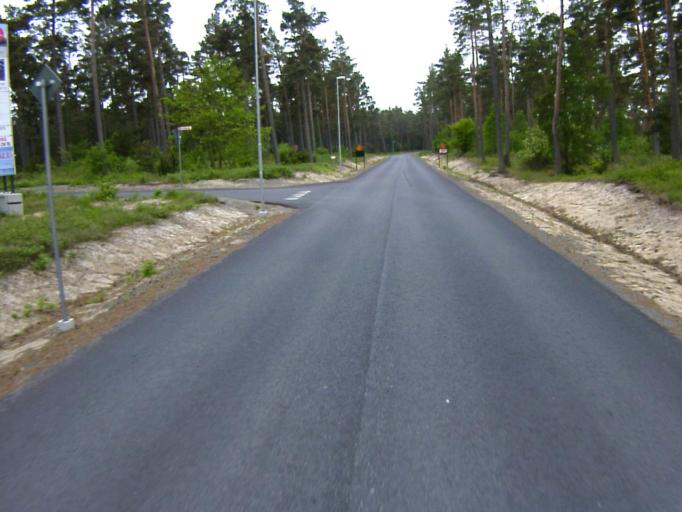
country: SE
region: Skane
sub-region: Kristianstads Kommun
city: Ahus
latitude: 55.9083
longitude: 14.2696
